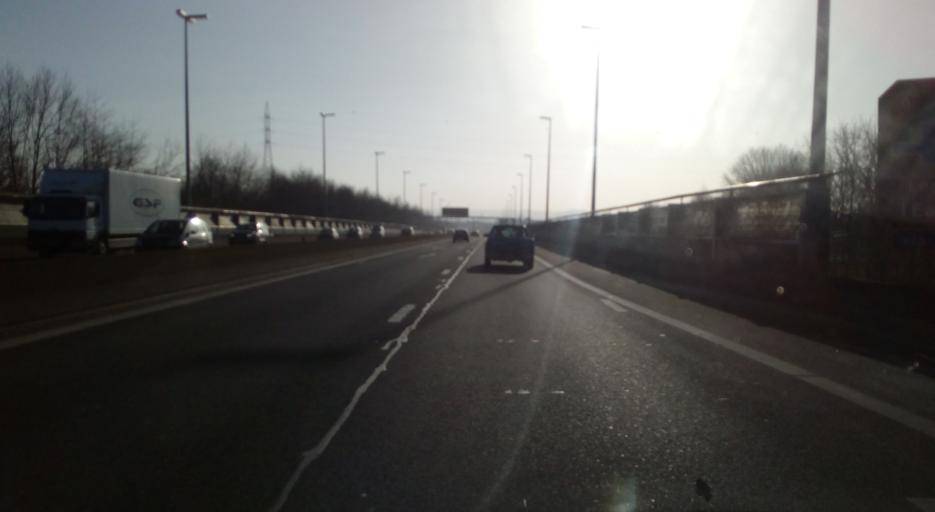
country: BE
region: Wallonia
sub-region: Province du Hainaut
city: Charleroi
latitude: 50.4475
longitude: 4.4423
